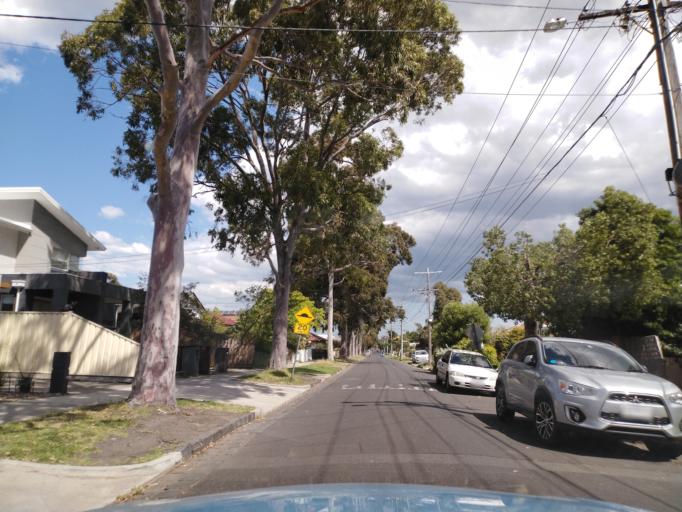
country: AU
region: Victoria
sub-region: Hobsons Bay
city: South Kingsville
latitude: -37.8344
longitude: 144.8686
